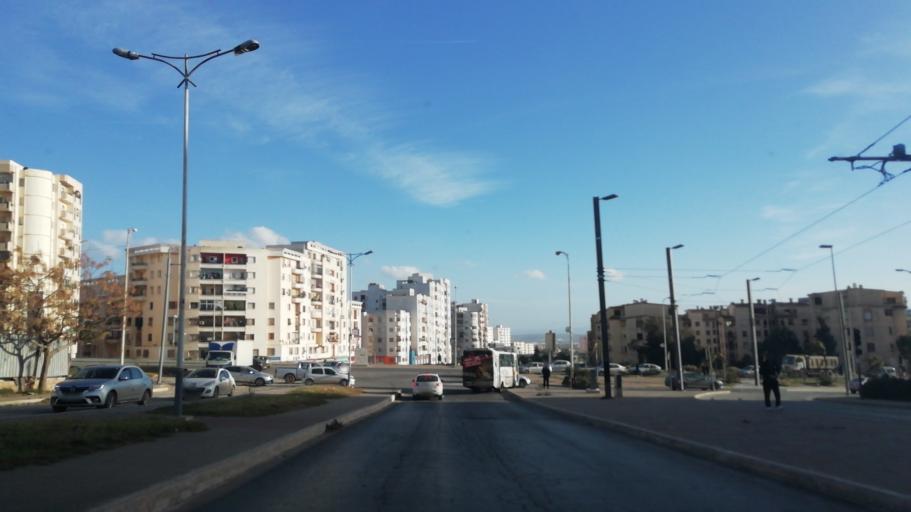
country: DZ
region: Oran
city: Bir el Djir
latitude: 35.7000
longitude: -0.5686
